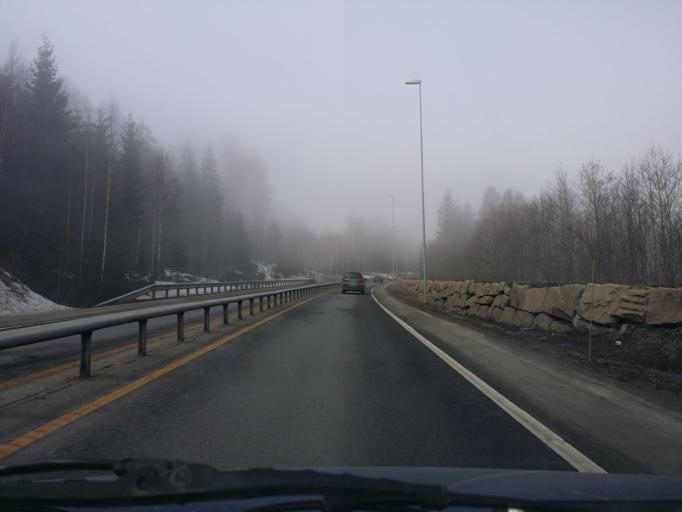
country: NO
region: Buskerud
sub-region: Drammen
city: Drammen
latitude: 59.7403
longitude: 10.1428
